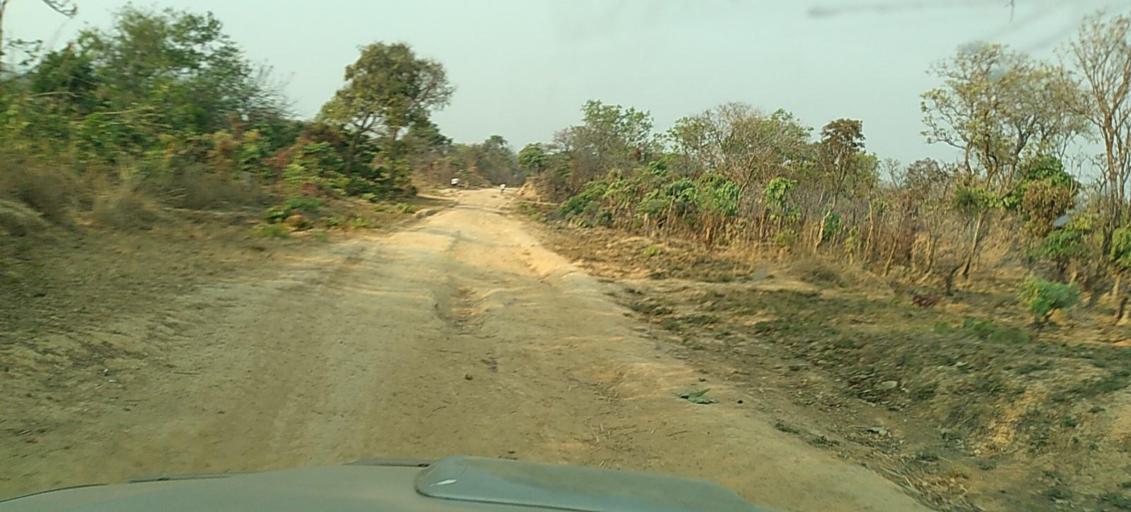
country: ZM
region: North-Western
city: Kasempa
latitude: -13.2709
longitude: 26.5580
